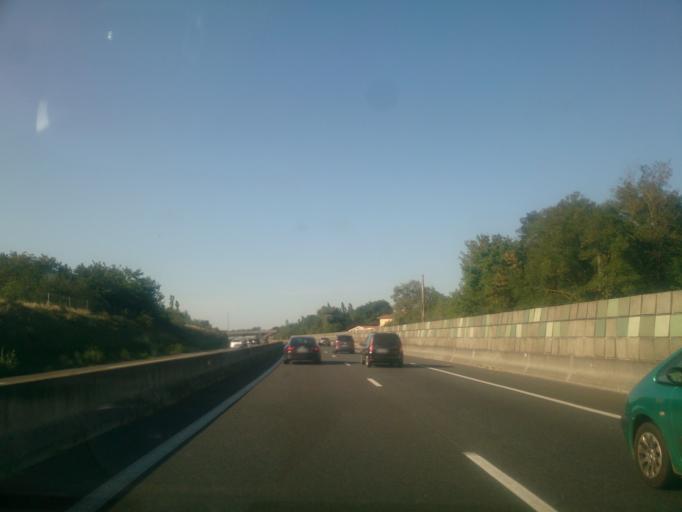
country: FR
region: Midi-Pyrenees
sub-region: Departement du Tarn-et-Garonne
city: Montauban
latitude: 44.0137
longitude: 1.3871
